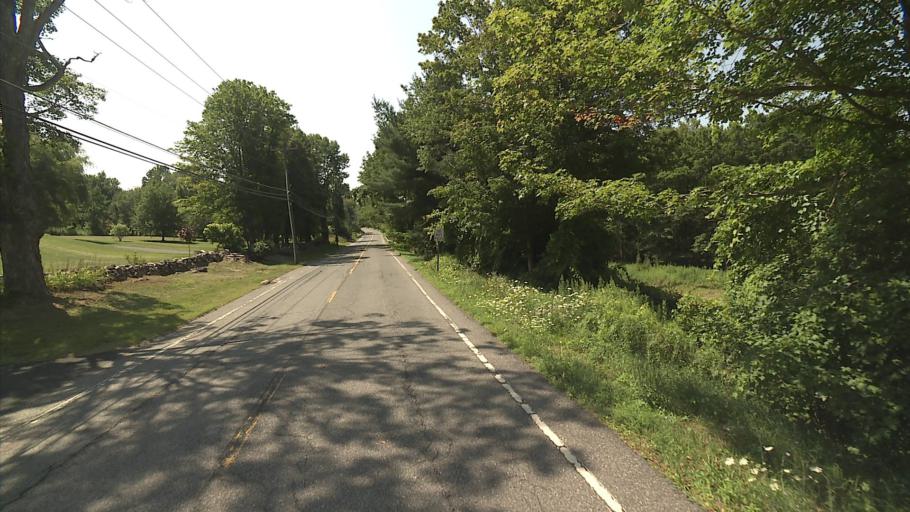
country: US
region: Connecticut
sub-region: Litchfield County
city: Winchester Center
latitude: 41.9713
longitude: -73.1999
